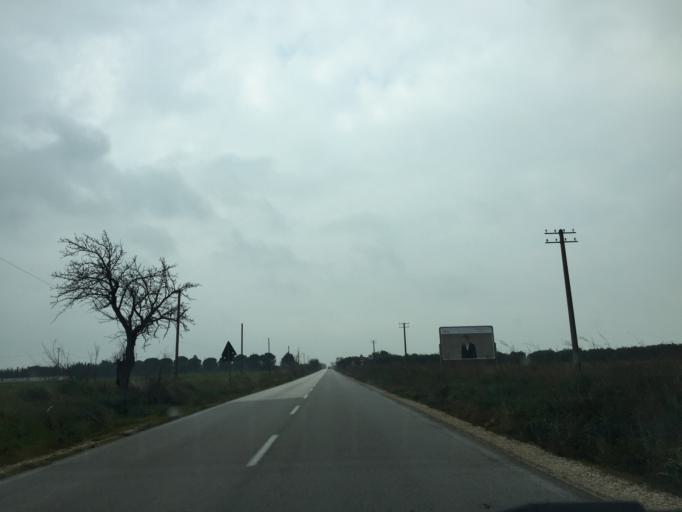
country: IT
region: Apulia
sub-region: Provincia di Foggia
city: Castelluccio dei Sauri
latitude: 41.4057
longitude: 15.4400
